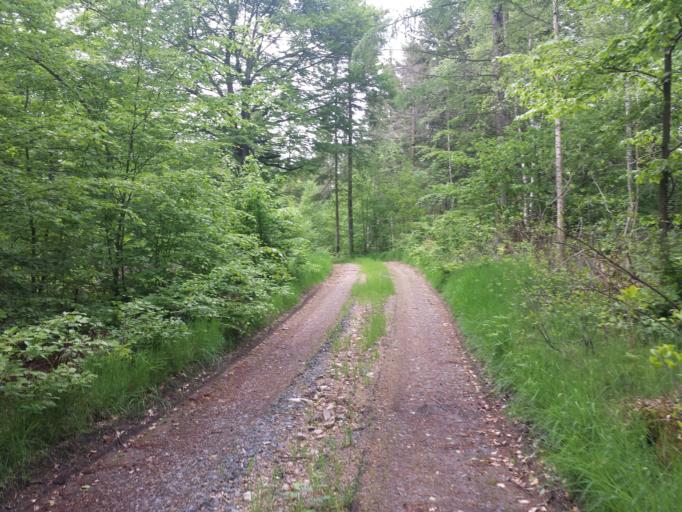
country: SE
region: Skane
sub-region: Hoors Kommun
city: Hoeoer
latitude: 55.9540
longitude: 13.5708
